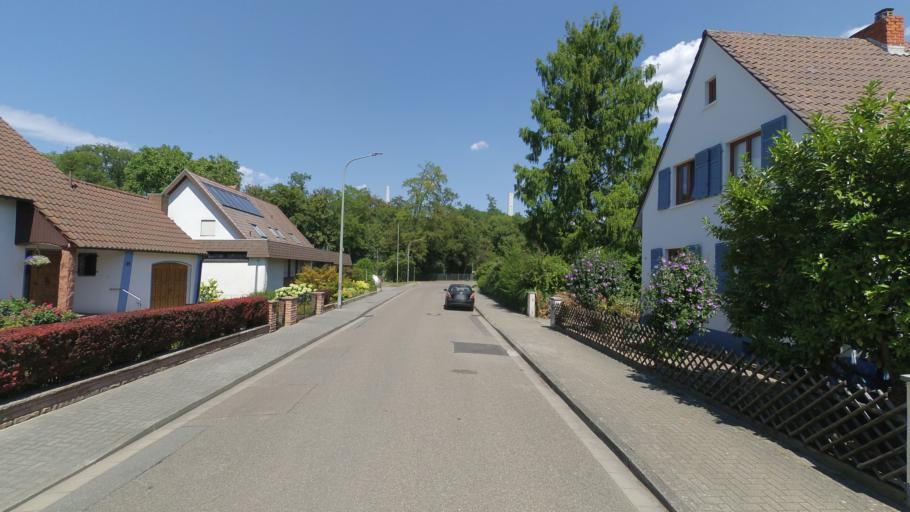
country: DE
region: Rheinland-Pfalz
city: Altrip
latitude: 49.4353
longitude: 8.4979
